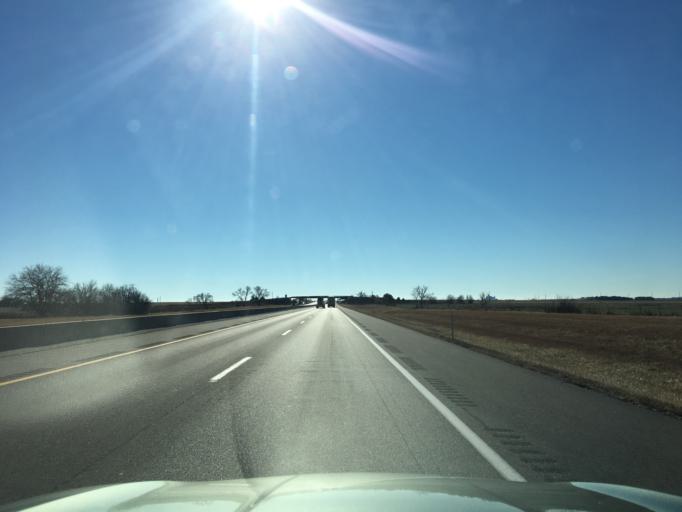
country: US
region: Kansas
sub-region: Sumner County
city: Wellington
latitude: 37.3095
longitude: -97.3406
